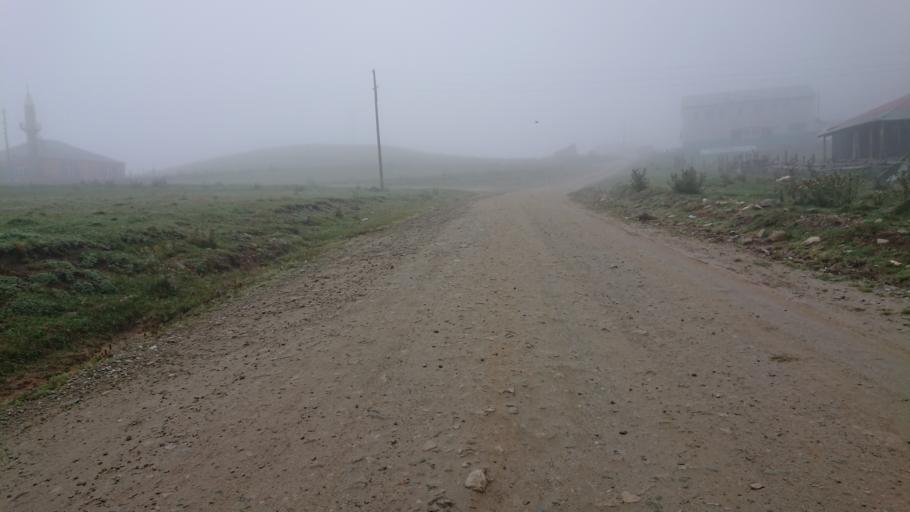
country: TR
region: Gumushane
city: Kurtun
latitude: 40.6726
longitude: 38.9951
